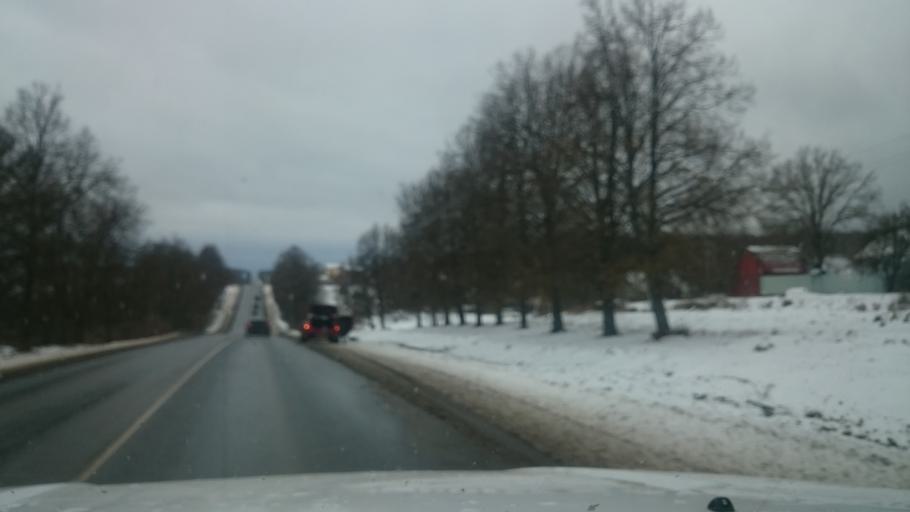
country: RU
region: Tula
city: Kosaya Gora
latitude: 54.1084
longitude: 37.5544
